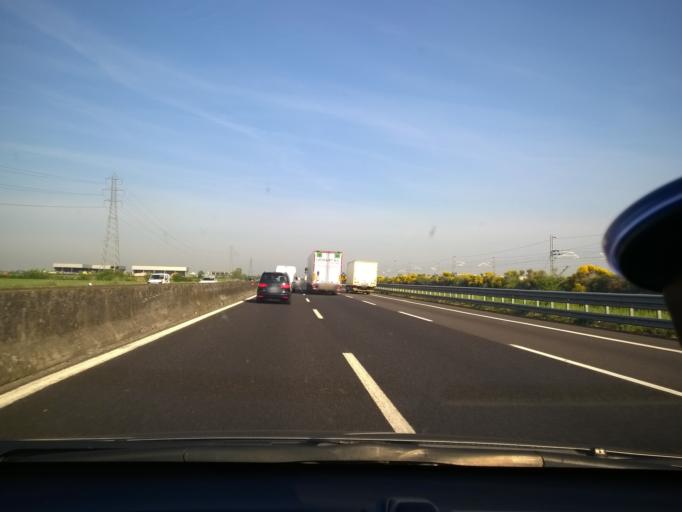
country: IT
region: Emilia-Romagna
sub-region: Provincia di Reggio Emilia
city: Prato
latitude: 44.7067
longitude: 10.7320
